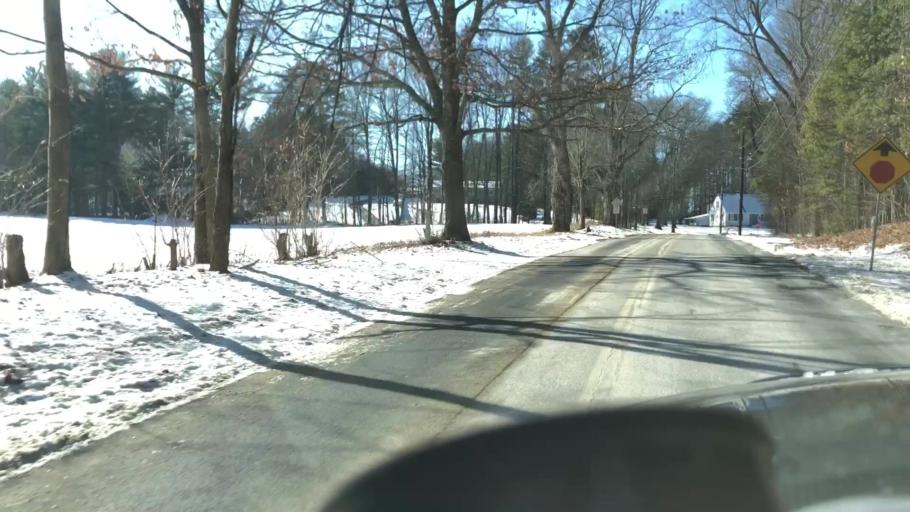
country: US
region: Massachusetts
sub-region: Hampshire County
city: Southampton
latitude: 42.2225
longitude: -72.7120
